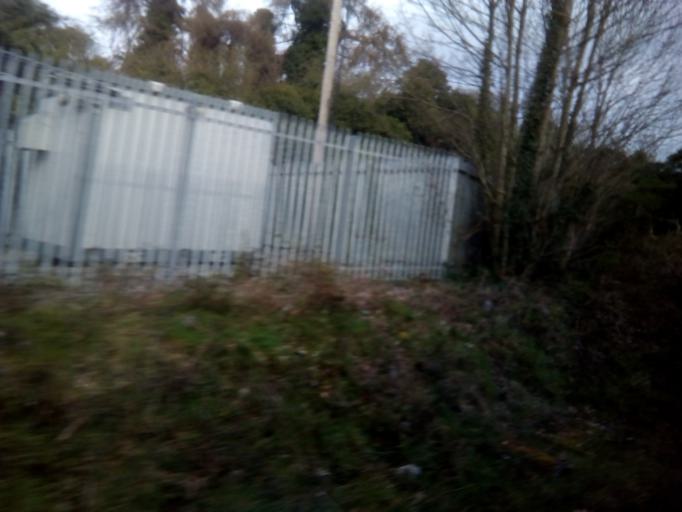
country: IE
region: Leinster
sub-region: Kildare
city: Kilcock
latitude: 53.4046
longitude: -6.6784
